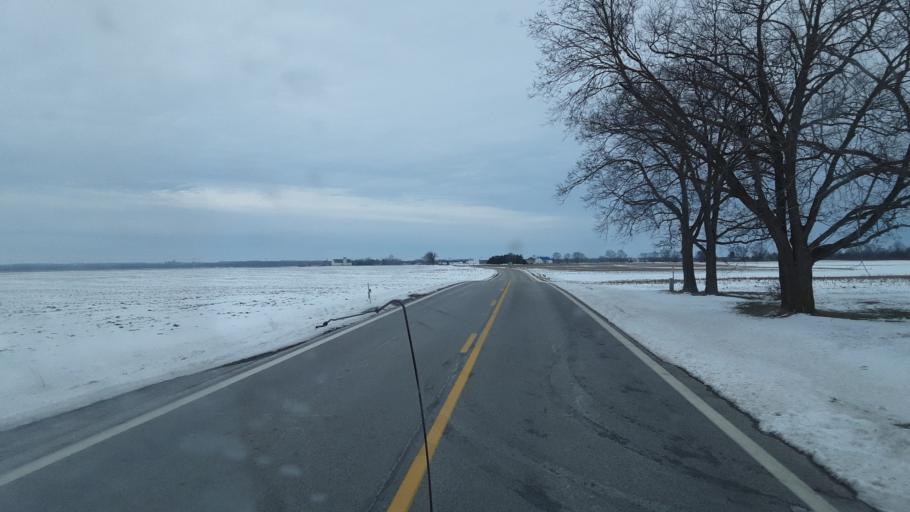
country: US
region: Ohio
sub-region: Pickaway County
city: Circleville
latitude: 39.6168
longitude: -83.0151
